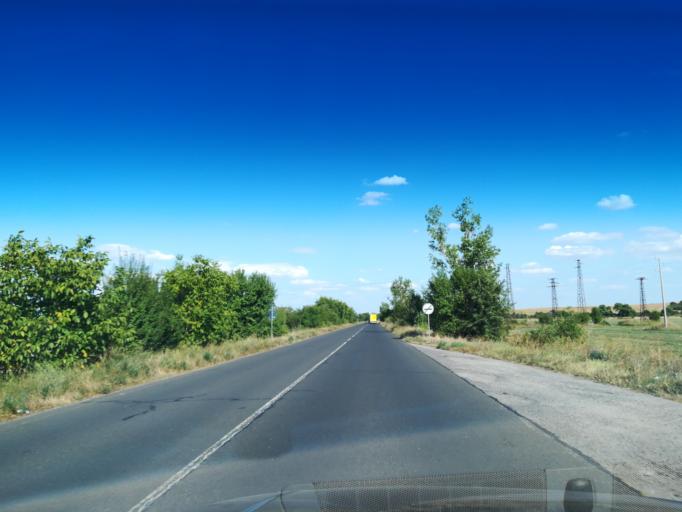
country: BG
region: Stara Zagora
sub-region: Obshtina Chirpan
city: Chirpan
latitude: 42.0716
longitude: 25.2028
